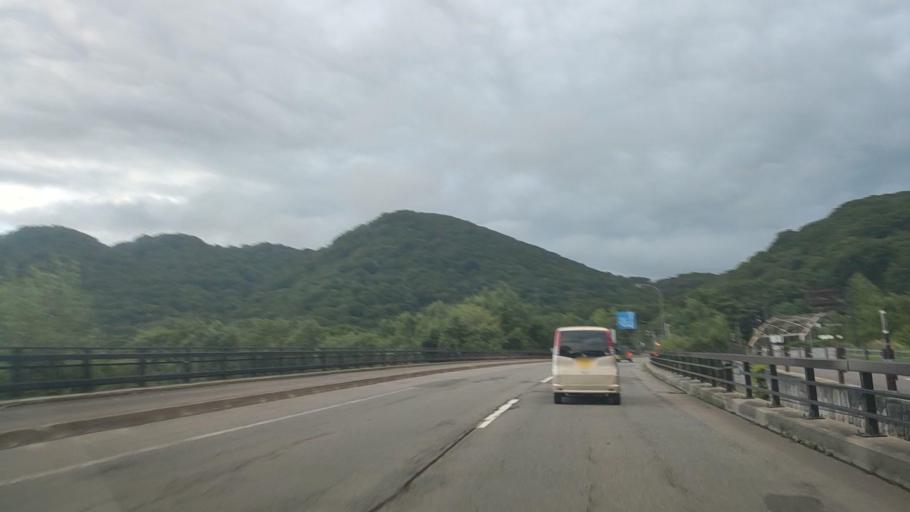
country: JP
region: Hokkaido
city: Nanae
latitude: 41.9580
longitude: 140.6498
